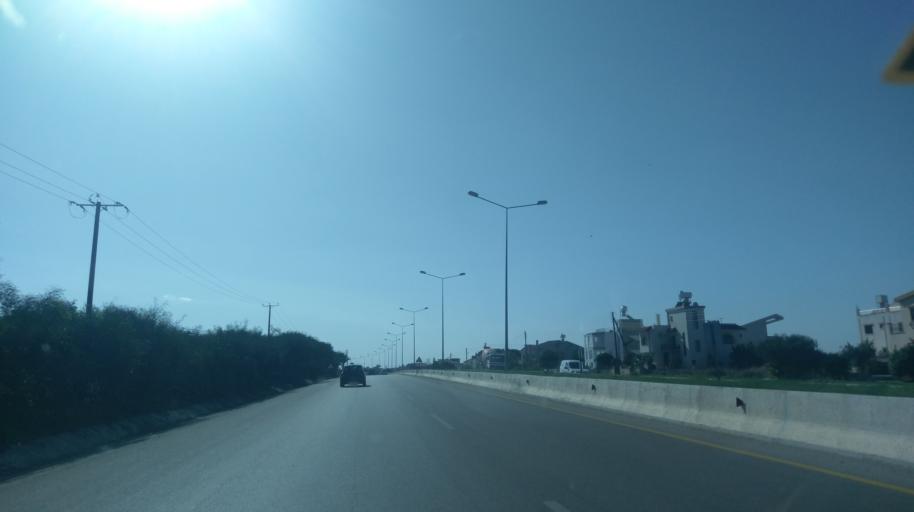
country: CY
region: Ammochostos
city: Trikomo
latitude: 35.2217
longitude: 33.8947
